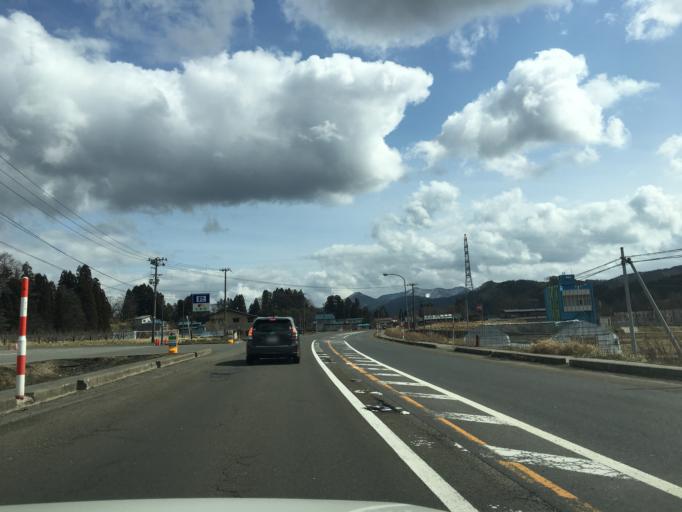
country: JP
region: Akita
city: Odate
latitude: 40.2282
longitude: 140.5978
